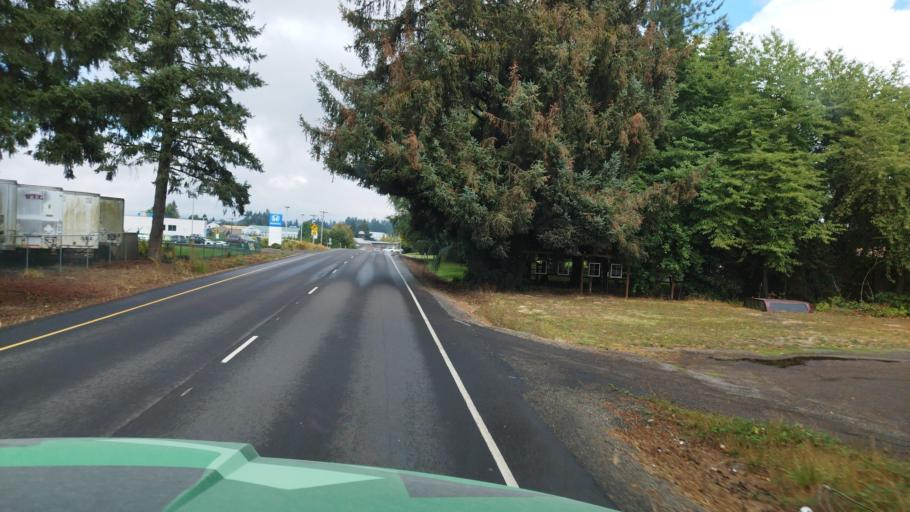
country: US
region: Oregon
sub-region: Yamhill County
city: Lafayette
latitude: 45.2353
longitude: -123.1514
